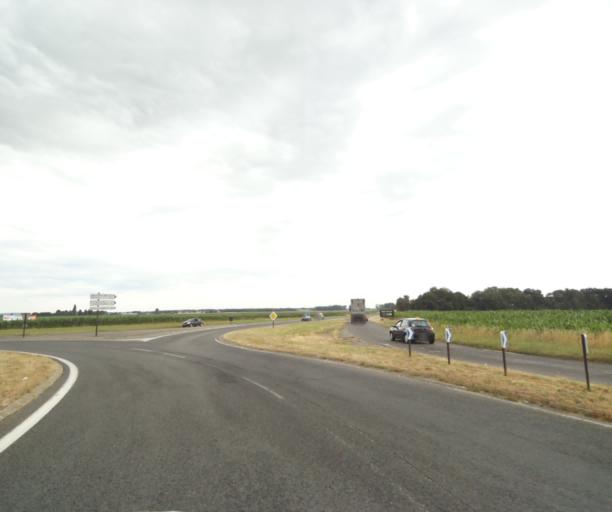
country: FR
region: Ile-de-France
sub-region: Departement de Seine-et-Marne
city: Pringy
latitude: 48.4943
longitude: 2.5845
